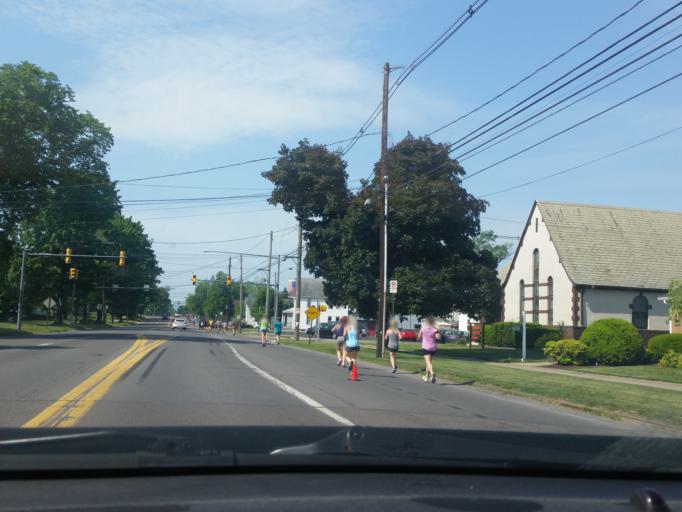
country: US
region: Pennsylvania
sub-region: Luzerne County
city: Swoyersville
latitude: 41.2951
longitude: -75.8650
